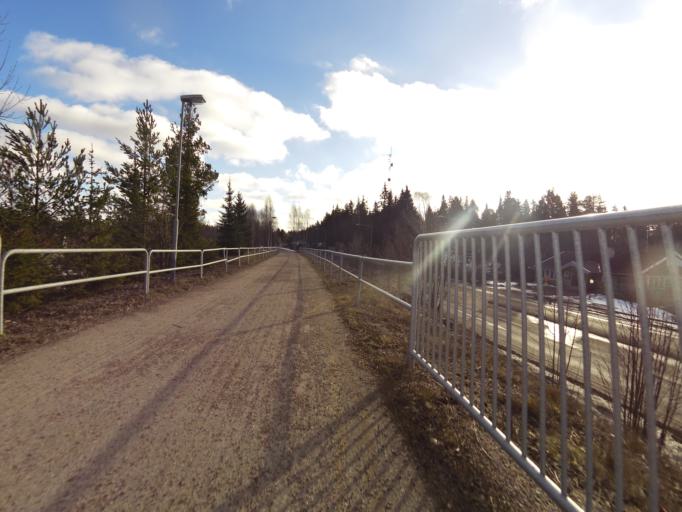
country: SE
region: Gaevleborg
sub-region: Gavle Kommun
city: Gavle
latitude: 60.6502
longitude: 17.1858
